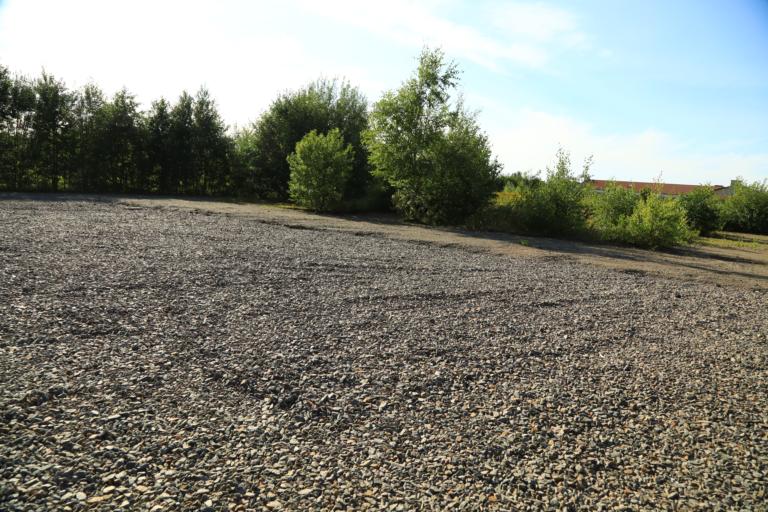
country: SE
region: Halland
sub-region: Varbergs Kommun
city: Varberg
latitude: 57.1536
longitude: 12.2558
